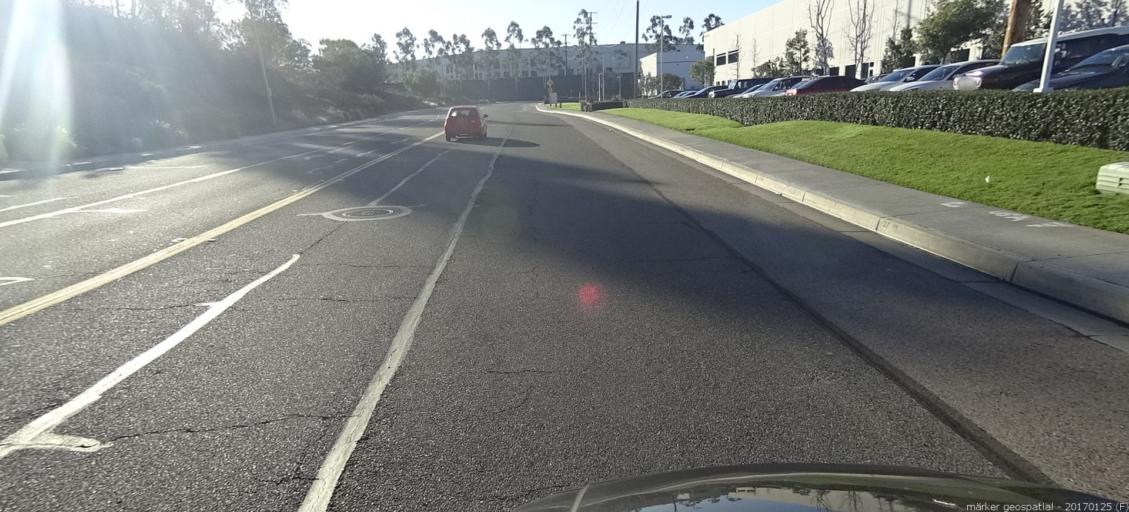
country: US
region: California
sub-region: Orange County
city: Portola Hills
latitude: 33.6712
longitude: -117.6486
